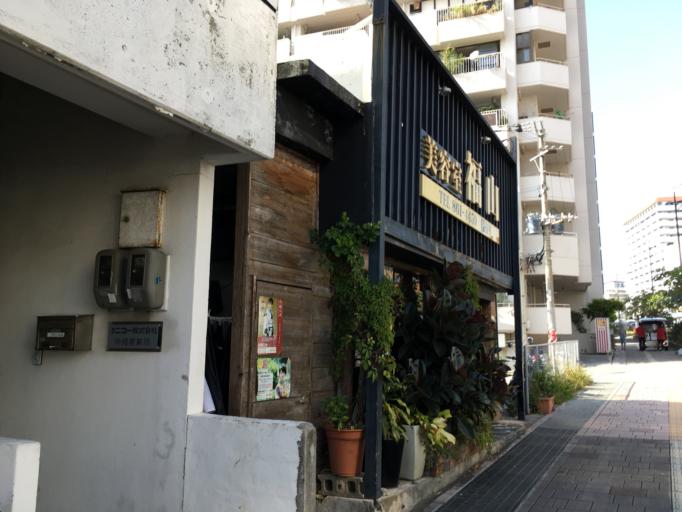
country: JP
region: Okinawa
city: Naha-shi
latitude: 26.2260
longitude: 127.6853
